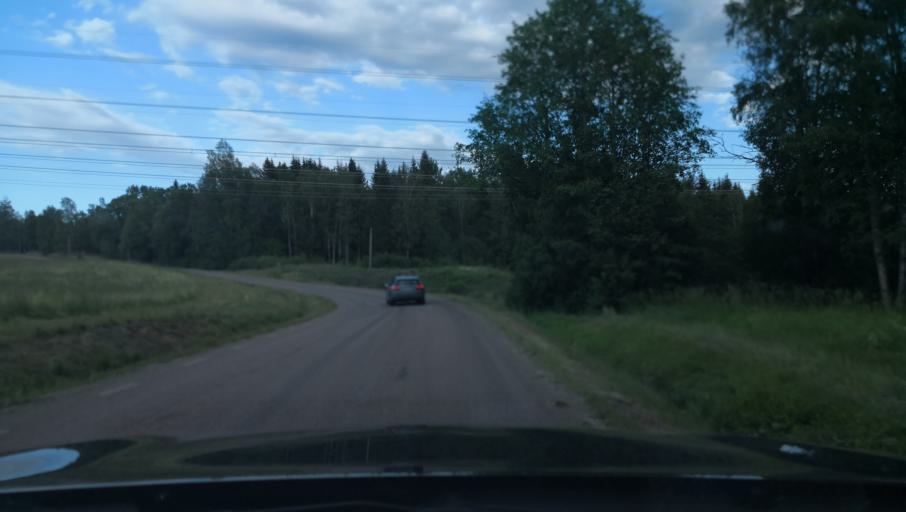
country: SE
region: Dalarna
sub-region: Ludvika Kommun
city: Ludvika
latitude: 60.0796
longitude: 15.2650
